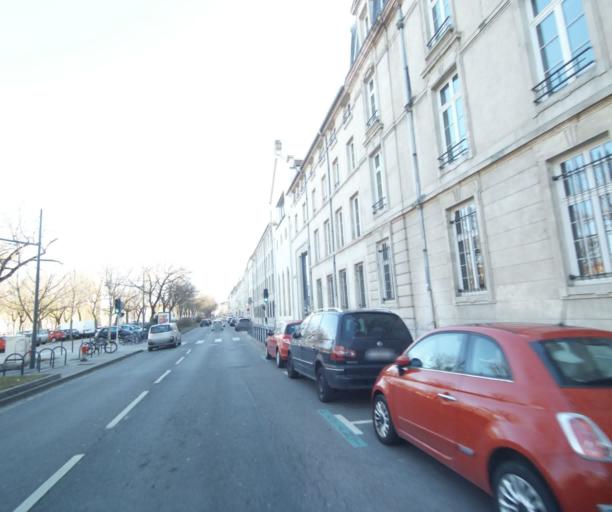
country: FR
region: Lorraine
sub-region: Departement de Meurthe-et-Moselle
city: Maxeville
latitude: 48.6955
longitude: 6.1751
